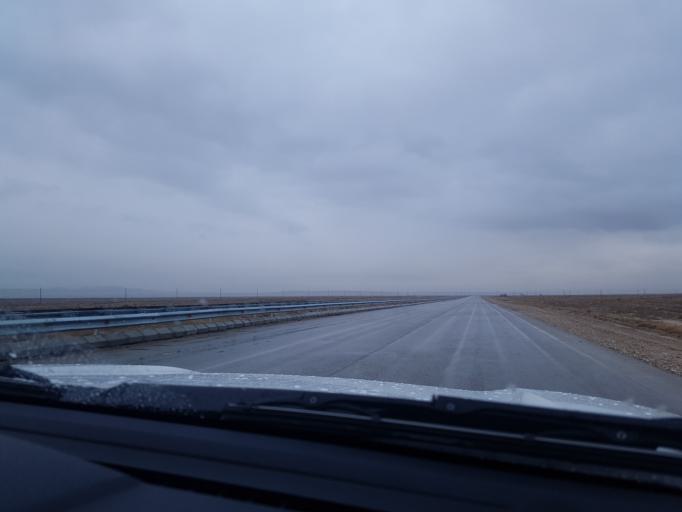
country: TM
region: Balkan
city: Turkmenbasy
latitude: 40.0674
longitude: 53.3413
